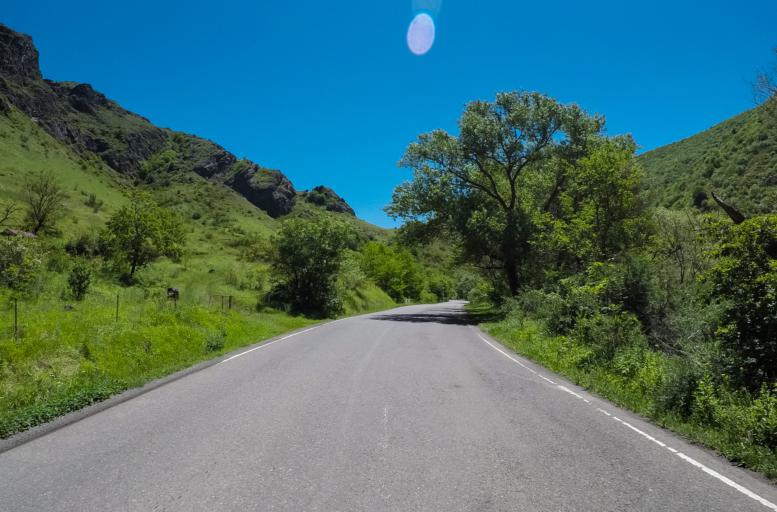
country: GE
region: Samtskhe-Javakheti
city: Akhaltsikhe
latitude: 41.6118
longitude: 43.0727
